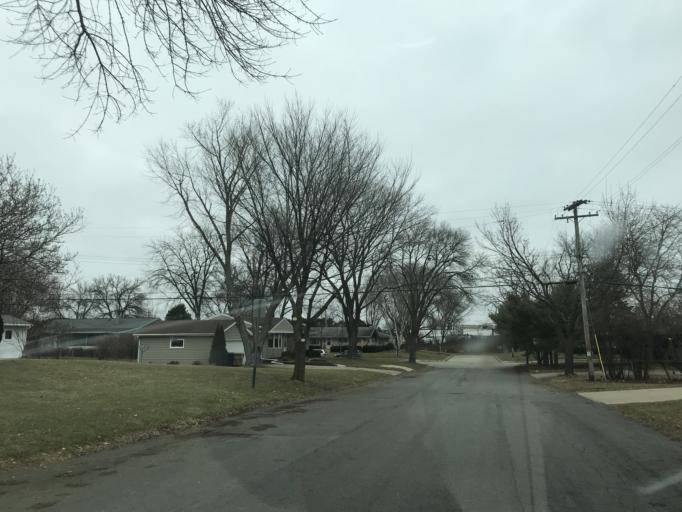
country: US
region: Wisconsin
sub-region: Dane County
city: Monona
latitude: 43.0640
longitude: -89.3131
